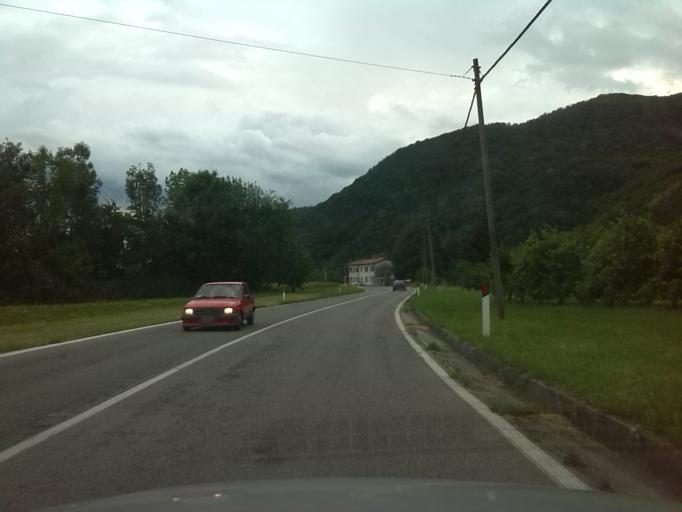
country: IT
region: Friuli Venezia Giulia
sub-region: Provincia di Udine
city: Pulfero
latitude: 46.1453
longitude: 13.4883
